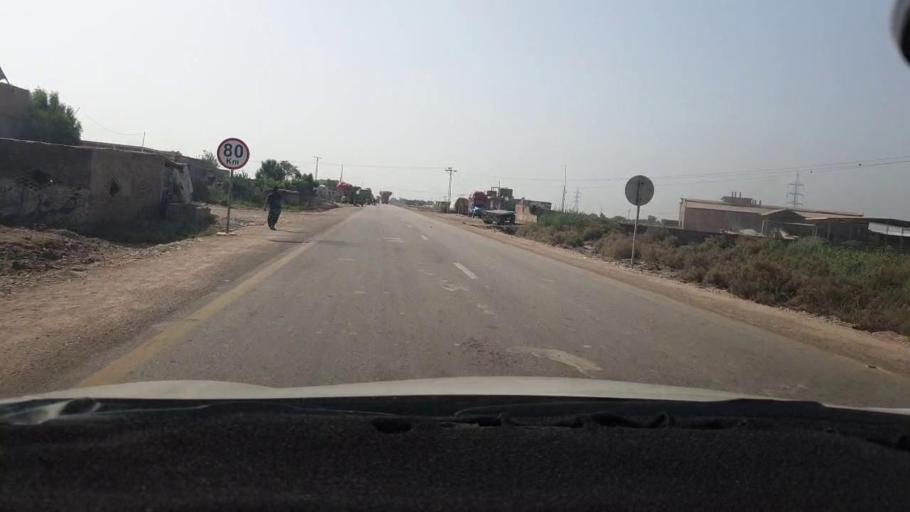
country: PK
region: Sindh
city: Sanghar
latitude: 25.9729
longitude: 68.9707
